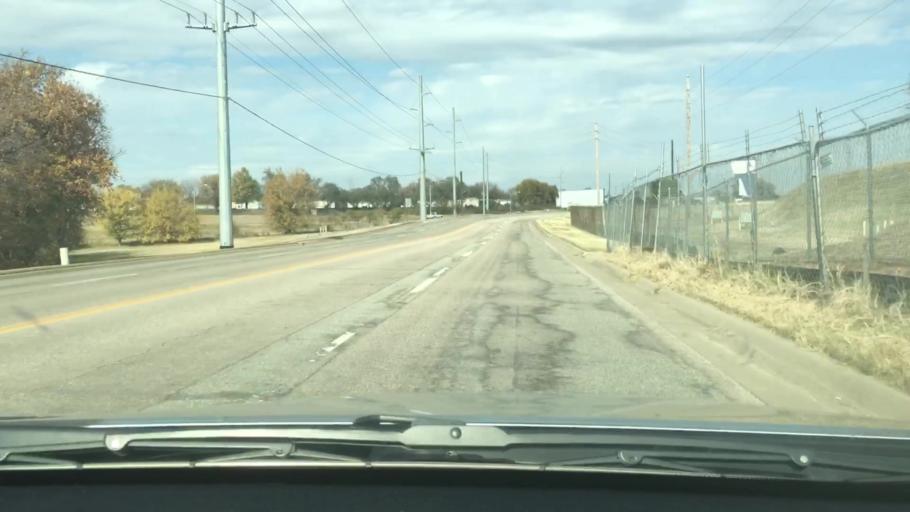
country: US
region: Kansas
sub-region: Sedgwick County
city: Wichita
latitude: 37.6265
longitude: -97.2897
